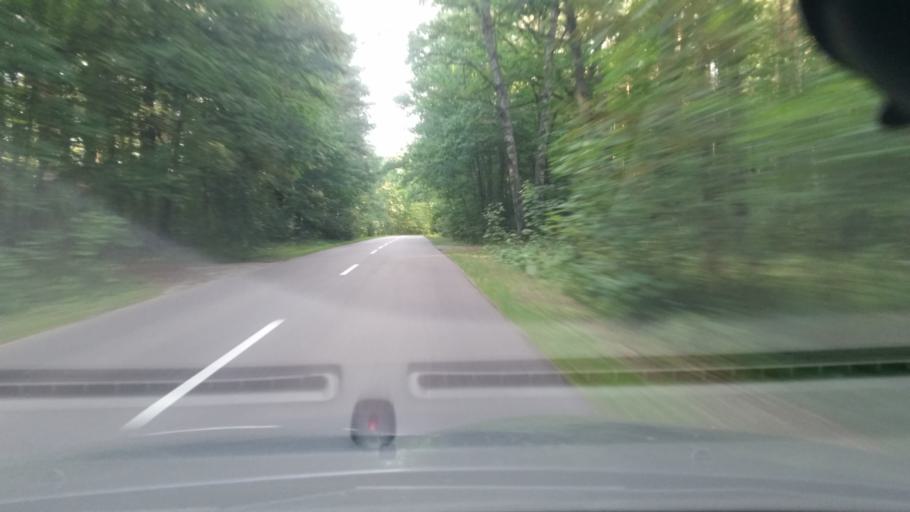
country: PL
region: Pomeranian Voivodeship
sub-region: Powiat wejherowski
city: Choczewo
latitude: 54.7541
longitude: 17.7476
